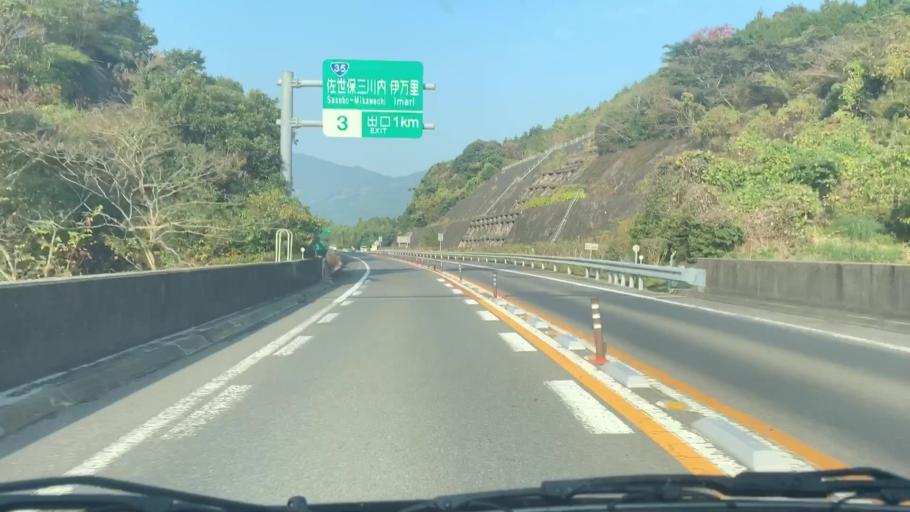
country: JP
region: Saga Prefecture
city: Imaricho-ko
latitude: 33.1655
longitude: 129.8605
